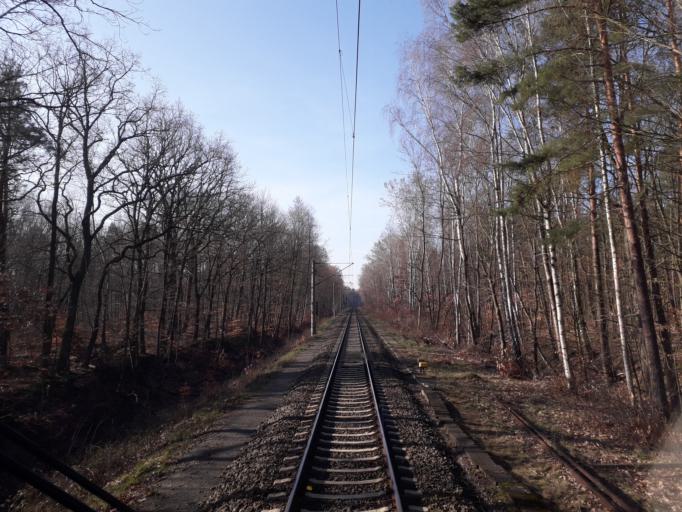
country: DE
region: Brandenburg
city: Michendorf
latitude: 52.3709
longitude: 13.0103
